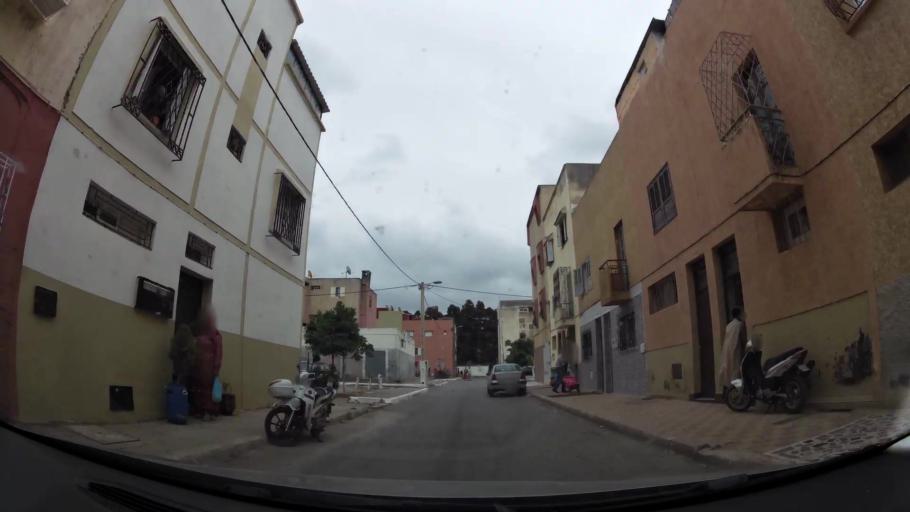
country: MA
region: Rabat-Sale-Zemmour-Zaer
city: Sale
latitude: 34.0444
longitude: -6.8005
